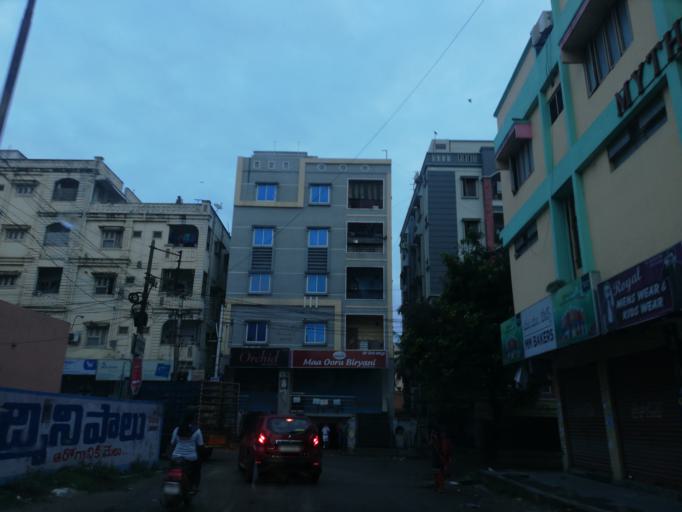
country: IN
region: Telangana
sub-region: Rangareddi
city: Kukatpalli
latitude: 17.4886
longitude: 78.3961
